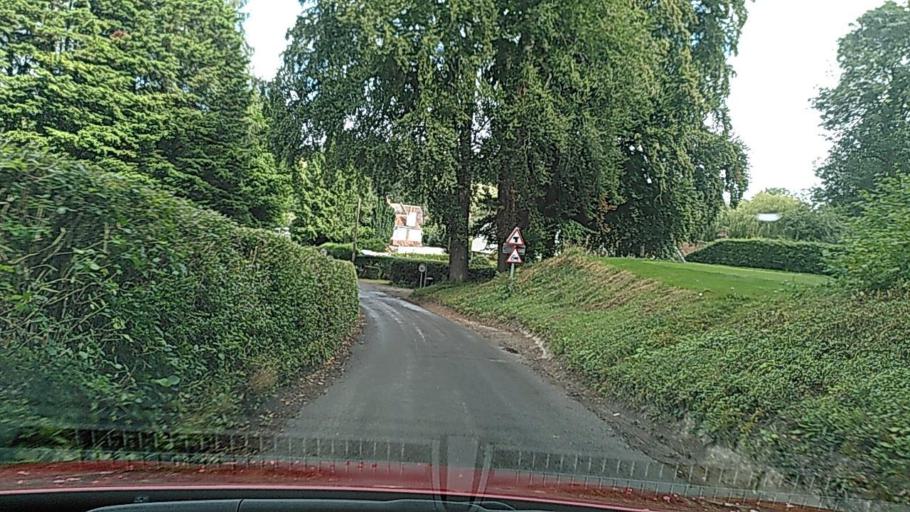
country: GB
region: England
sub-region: Oxfordshire
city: Henley on Thames
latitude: 51.5209
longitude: -0.9137
